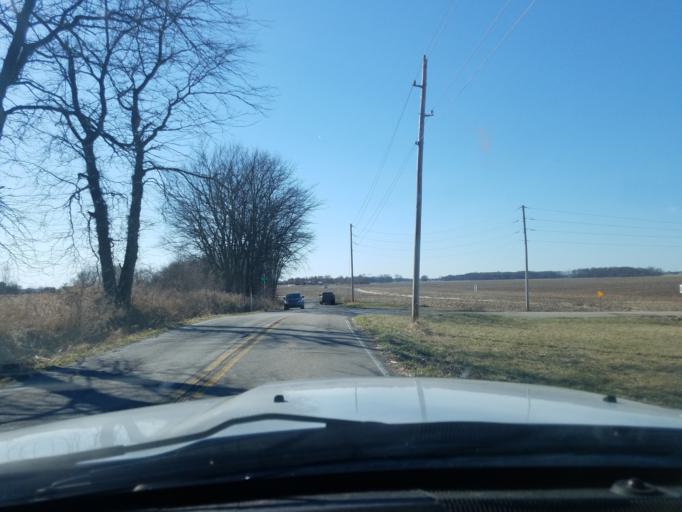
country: US
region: Indiana
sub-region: Johnson County
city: Franklin
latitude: 39.4955
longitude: -85.9703
